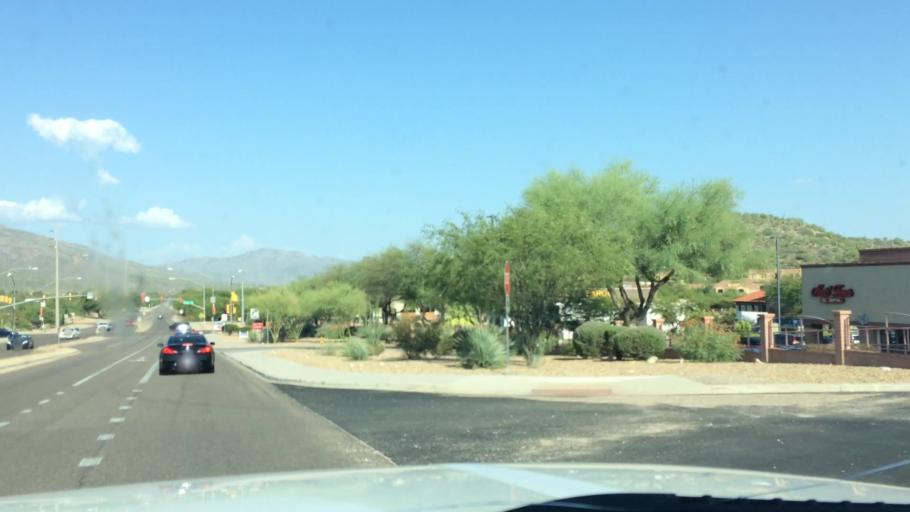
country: US
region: Arizona
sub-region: Pima County
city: Catalina Foothills
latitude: 32.3087
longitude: -110.8462
